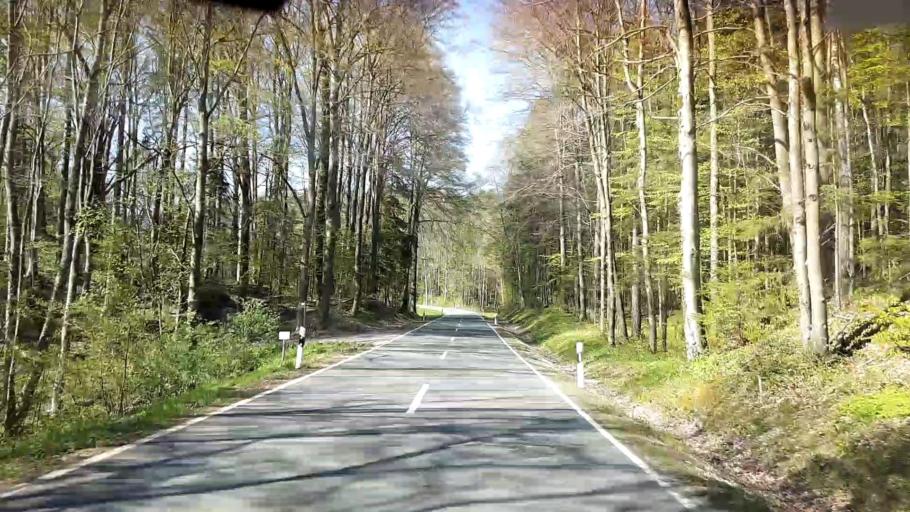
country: DE
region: Bavaria
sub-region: Upper Franconia
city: Pottenstein
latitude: 49.7948
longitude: 11.4082
